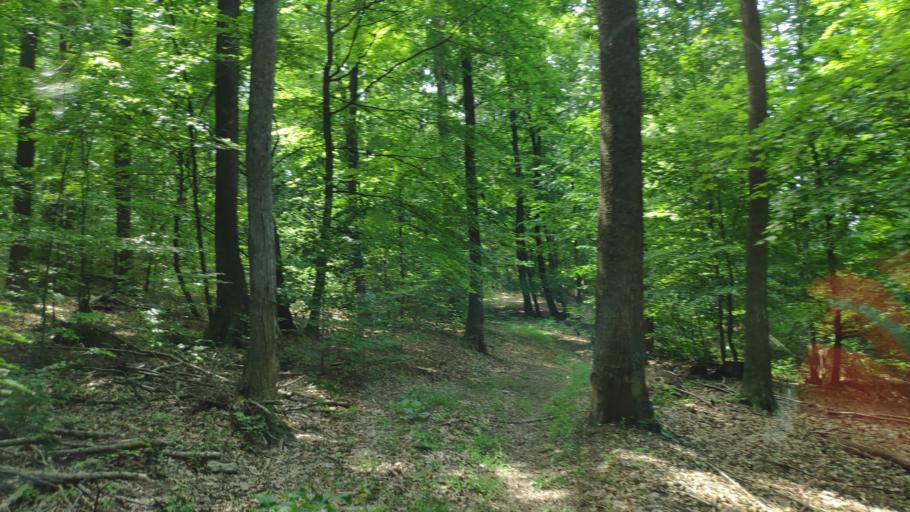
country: SK
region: Kosicky
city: Dobsina
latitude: 48.7060
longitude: 20.3873
